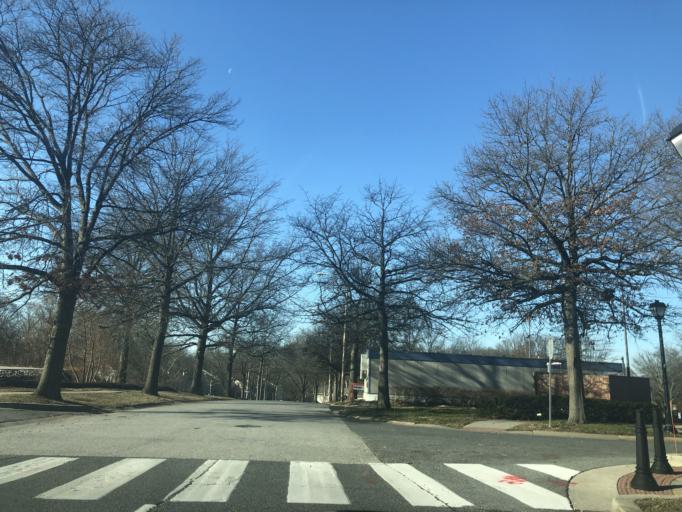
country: US
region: Maryland
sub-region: Howard County
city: Columbia
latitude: 39.2097
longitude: -76.8462
